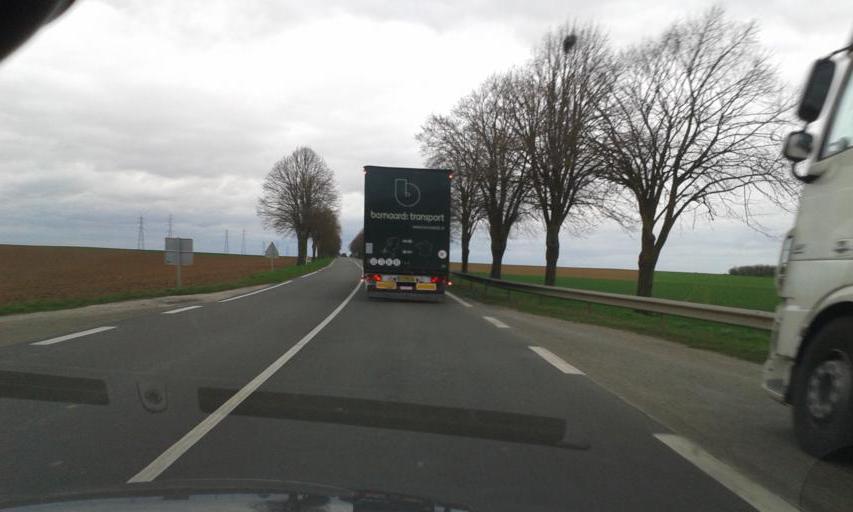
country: FR
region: Centre
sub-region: Departement d'Eure-et-Loir
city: Baigneaux
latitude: 48.1370
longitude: 1.8509
